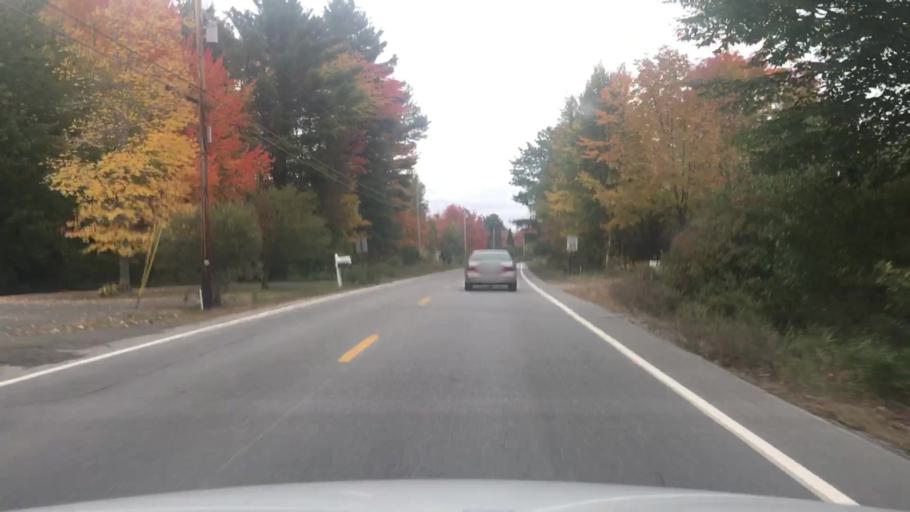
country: US
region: Maine
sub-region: Kennebec County
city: Oakland
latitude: 44.5373
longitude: -69.7920
